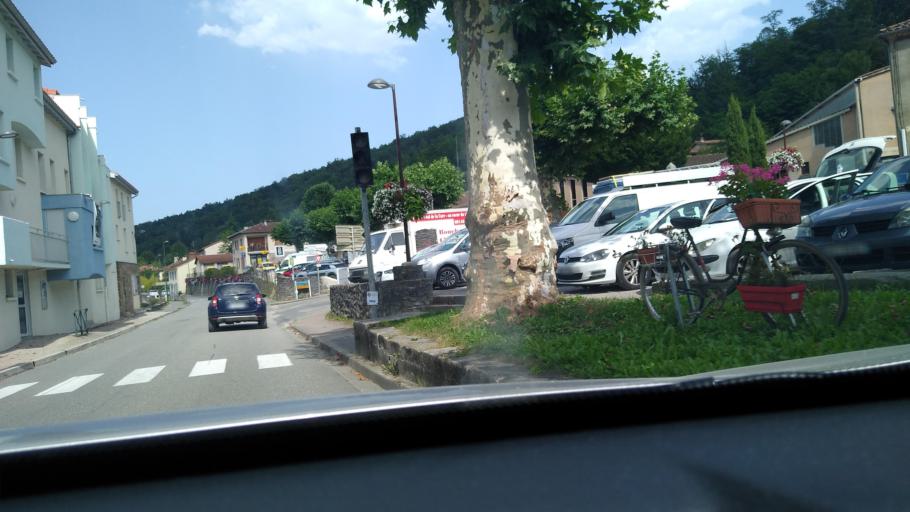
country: FR
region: Midi-Pyrenees
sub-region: Departement de l'Ariege
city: Saint-Girons
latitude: 42.8636
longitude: 1.2022
